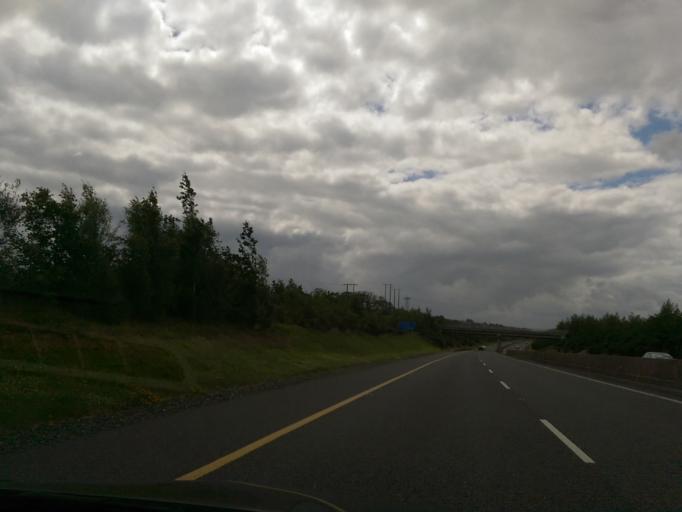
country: IE
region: Munster
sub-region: County Cork
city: Mitchelstown
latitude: 52.2583
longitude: -8.2520
